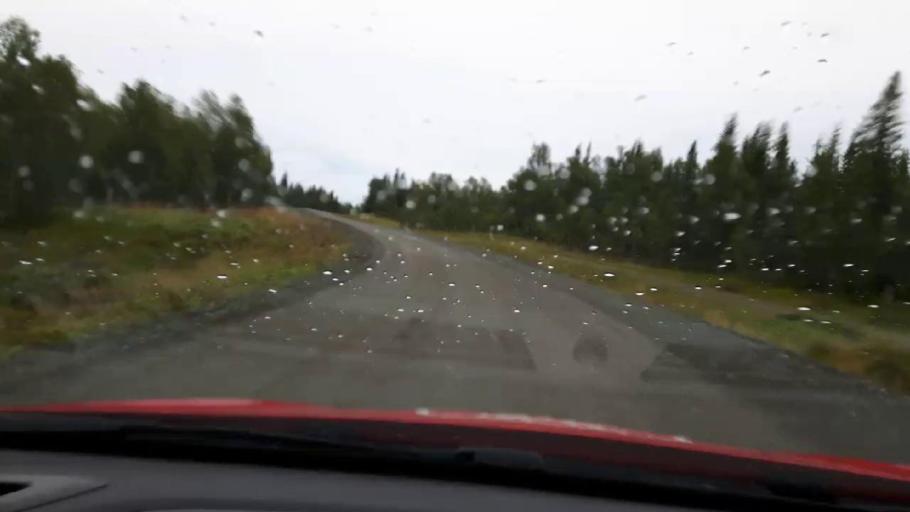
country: NO
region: Nord-Trondelag
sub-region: Meraker
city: Meraker
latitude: 63.5602
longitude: 12.2963
